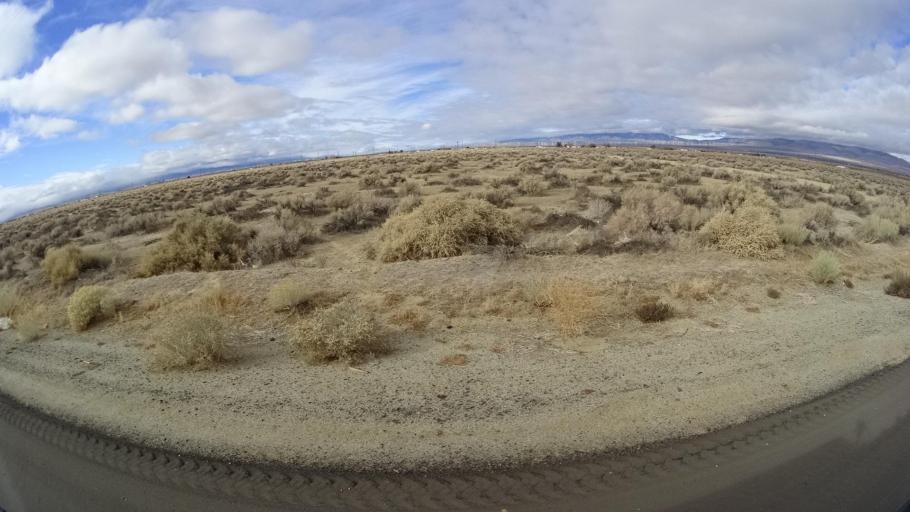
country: US
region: California
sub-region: Kern County
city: Rosamond
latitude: 34.8563
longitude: -118.2910
